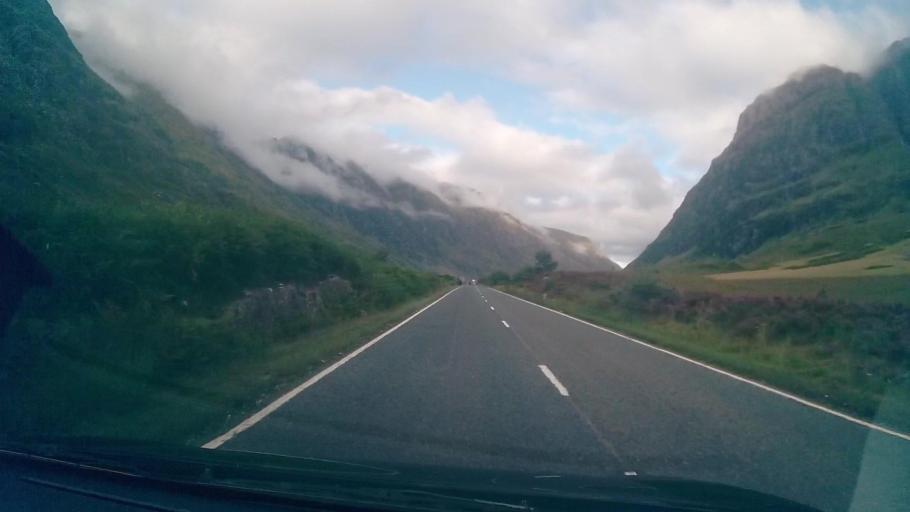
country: GB
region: Scotland
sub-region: Highland
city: Fort William
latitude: 56.6628
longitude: -5.0475
